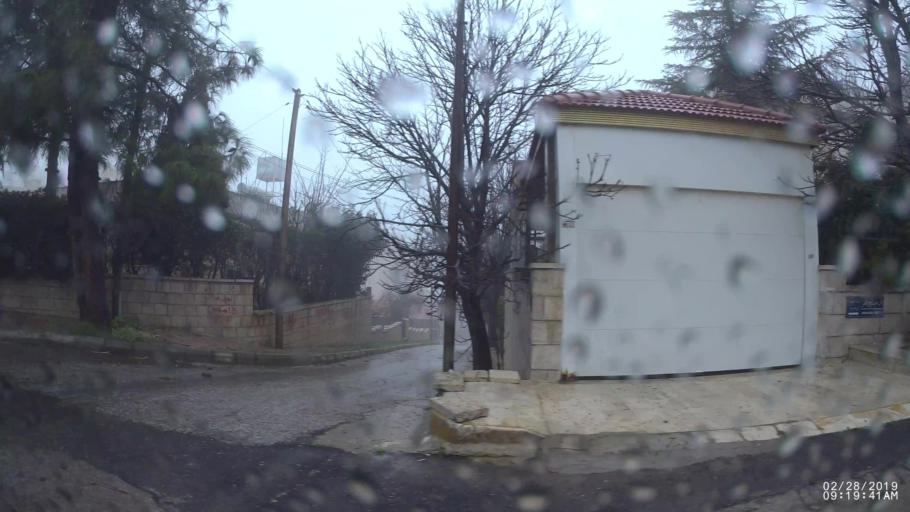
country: JO
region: Amman
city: Al Jubayhah
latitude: 32.0112
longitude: 35.8813
